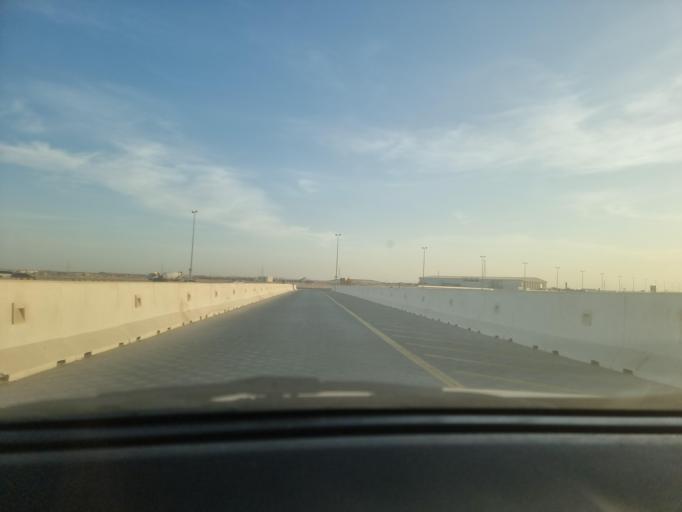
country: AE
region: Abu Dhabi
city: Abu Dhabi
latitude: 24.3152
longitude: 54.6775
